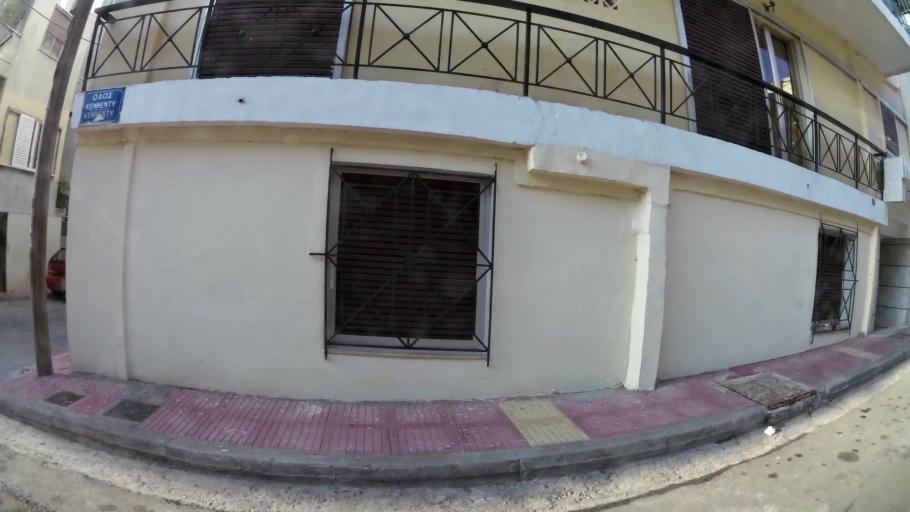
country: GR
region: Attica
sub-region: Nomarchia Athinas
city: Nea Filadelfeia
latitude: 38.0430
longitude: 23.7318
